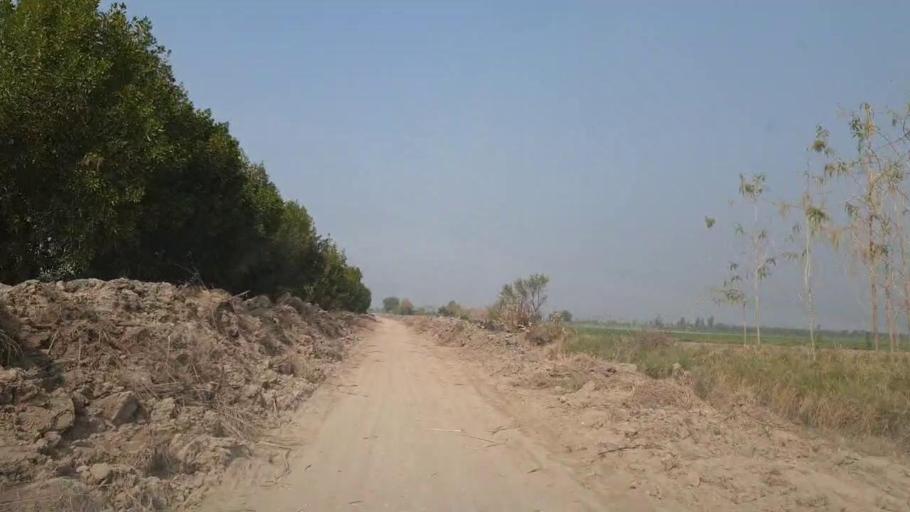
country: PK
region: Sindh
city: Mirpur Khas
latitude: 25.5619
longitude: 69.1437
